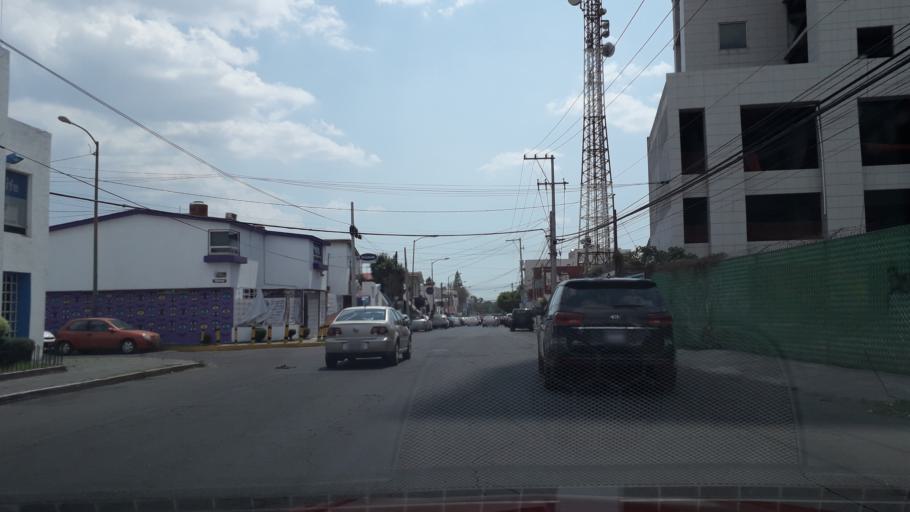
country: MX
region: Puebla
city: Puebla
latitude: 19.0342
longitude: -98.2217
